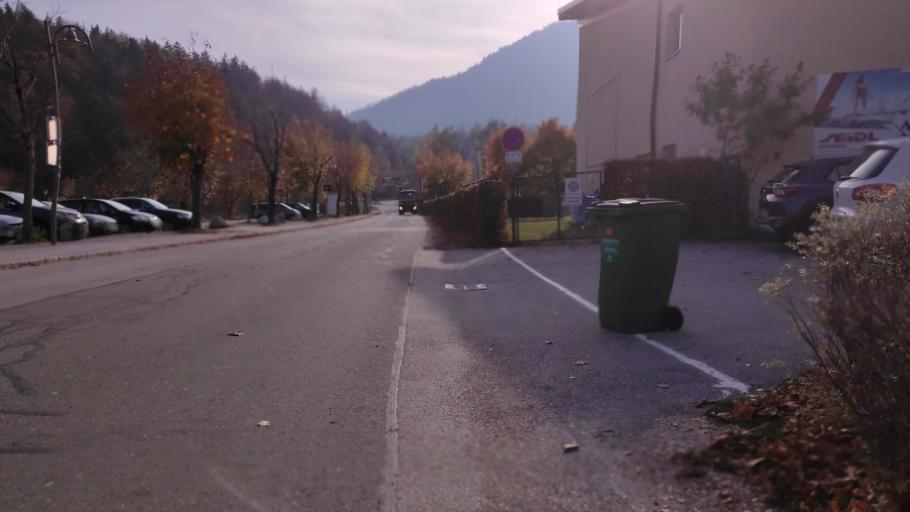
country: AT
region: Salzburg
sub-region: Politischer Bezirk Salzburg-Umgebung
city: Fuschl am See
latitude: 47.7942
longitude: 13.2996
